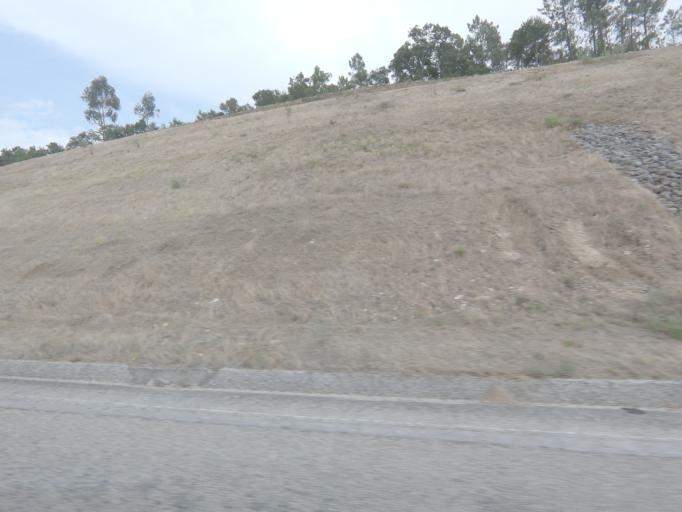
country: PT
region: Coimbra
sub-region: Coimbra
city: Coimbra
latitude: 40.2022
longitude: -8.4530
